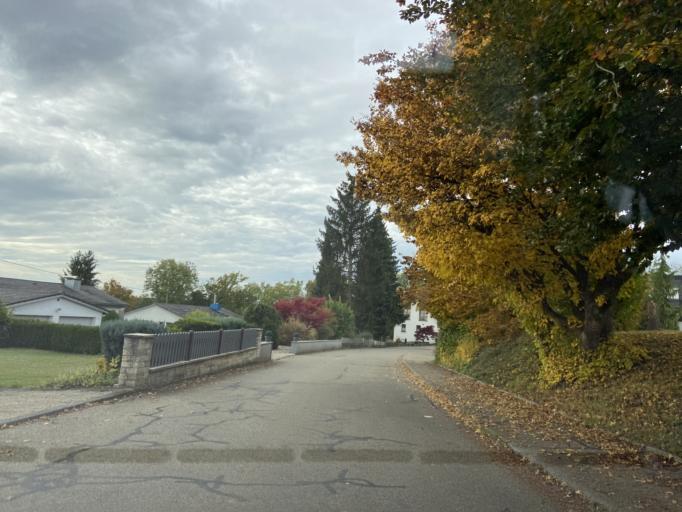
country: DE
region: Baden-Wuerttemberg
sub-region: Tuebingen Region
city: Bingen
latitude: 48.1130
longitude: 9.2650
